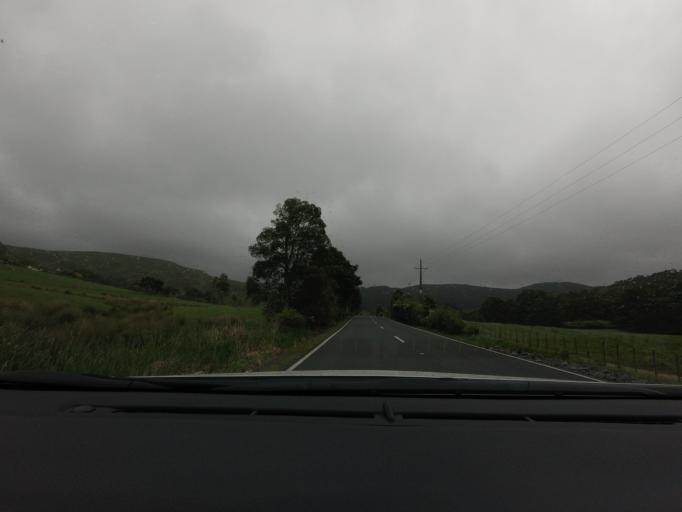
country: NZ
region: Auckland
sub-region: Auckland
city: Wellsford
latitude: -36.2900
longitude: 174.6269
